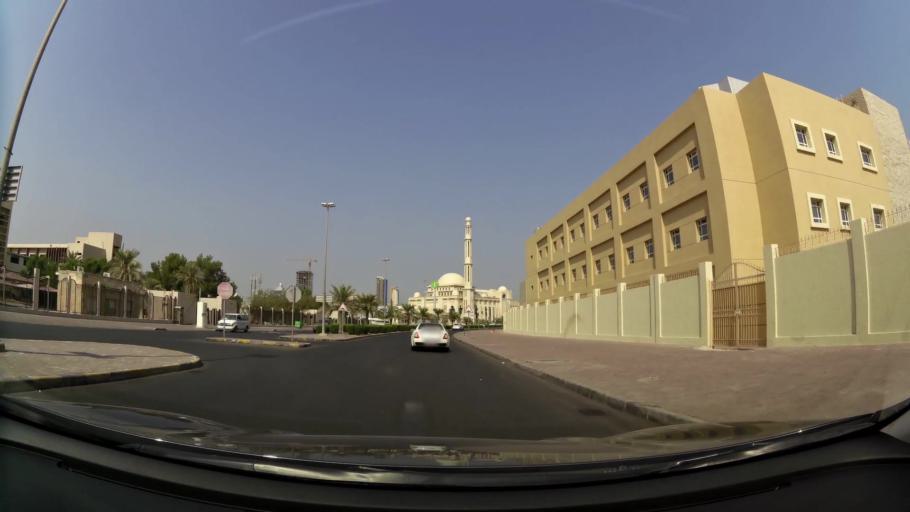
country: KW
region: Al Asimah
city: Ad Dasmah
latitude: 29.3589
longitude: 48.0119
